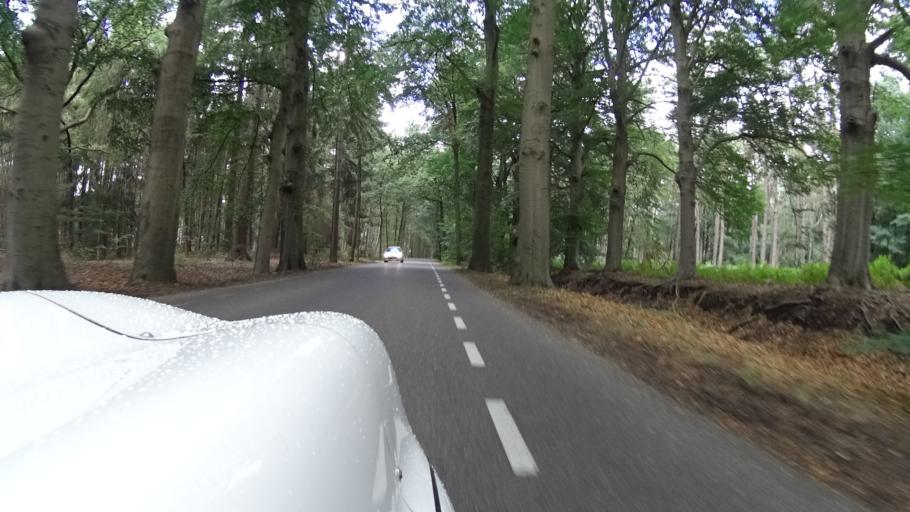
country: NL
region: Utrecht
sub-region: Gemeente Soest
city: Soest
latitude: 52.1680
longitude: 5.2233
